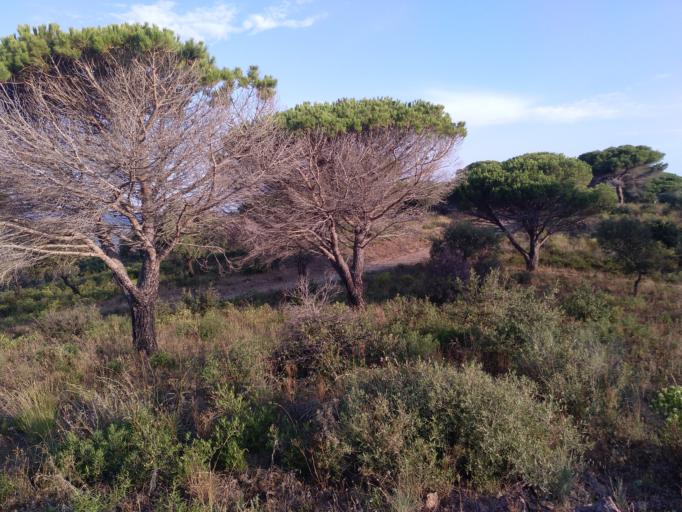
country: FR
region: Provence-Alpes-Cote d'Azur
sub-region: Departement du Var
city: Ramatuelle
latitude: 43.1859
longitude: 6.6158
